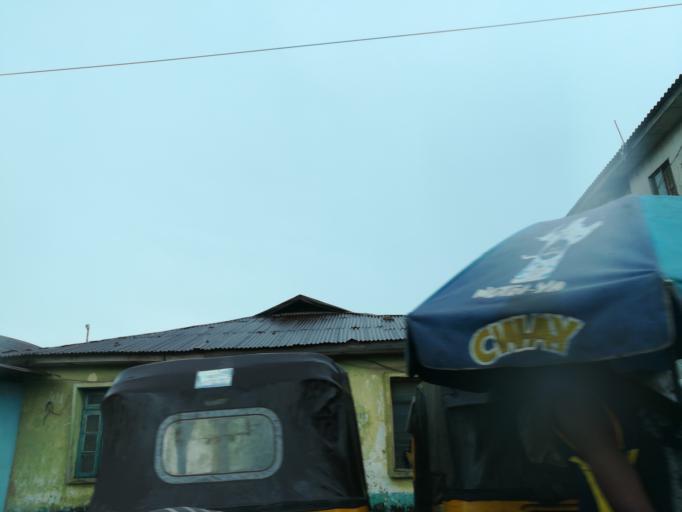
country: NG
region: Lagos
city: Oshodi
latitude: 6.5578
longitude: 3.3438
